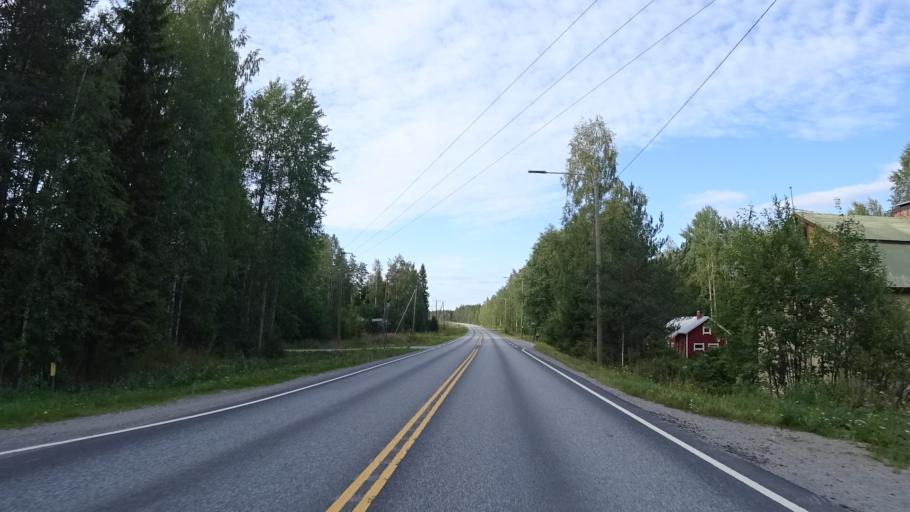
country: FI
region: North Karelia
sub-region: Joensuu
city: Eno
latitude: 62.8653
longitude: 30.2002
